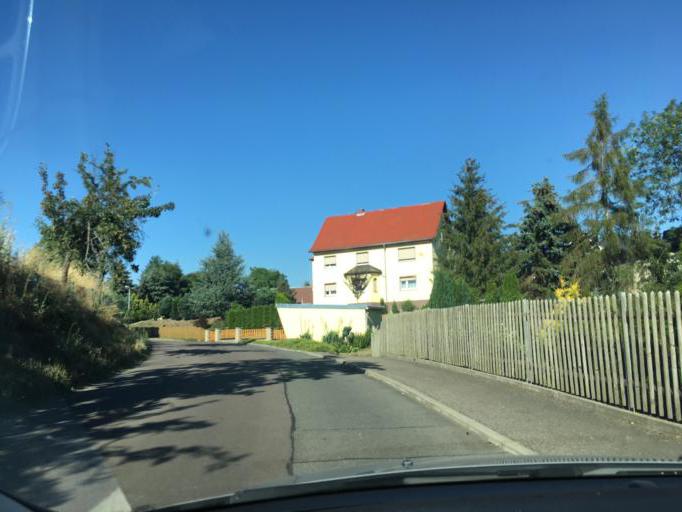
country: DE
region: Saxony
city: Frohburg
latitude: 51.0699
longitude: 12.5379
